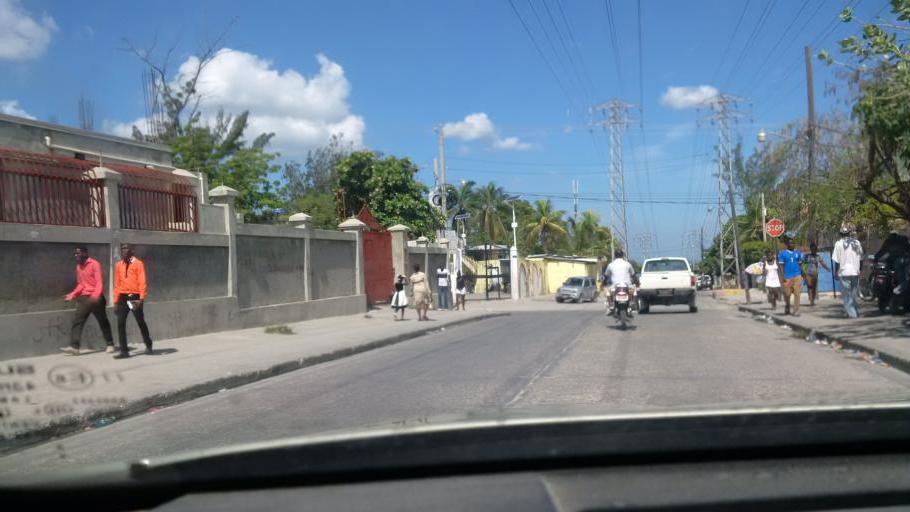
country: HT
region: Ouest
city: Delmas 73
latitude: 18.5588
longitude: -72.3018
